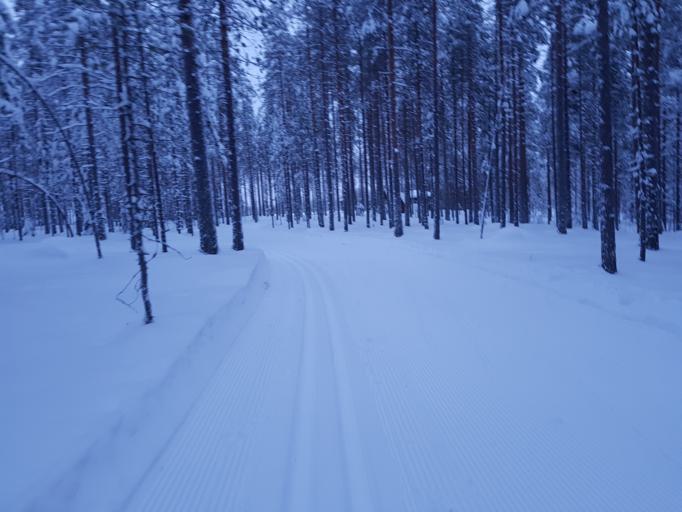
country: FI
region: Kainuu
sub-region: Kehys-Kainuu
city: Kuhmo
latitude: 64.0842
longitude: 29.5226
